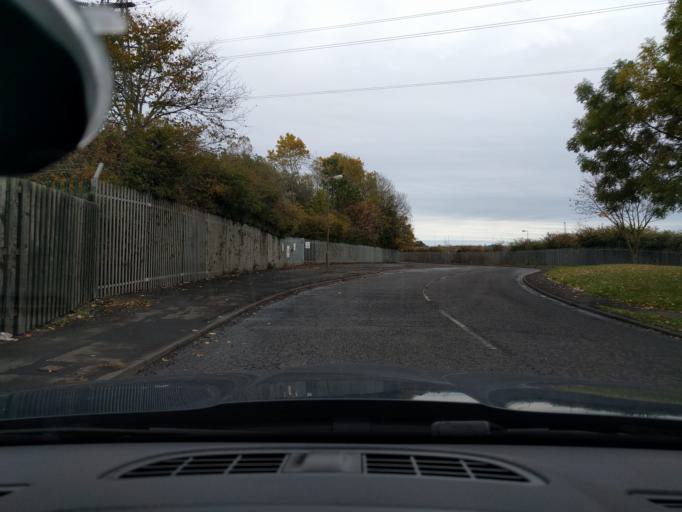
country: GB
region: England
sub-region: Northumberland
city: Blyth
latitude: 55.1443
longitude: -1.5322
